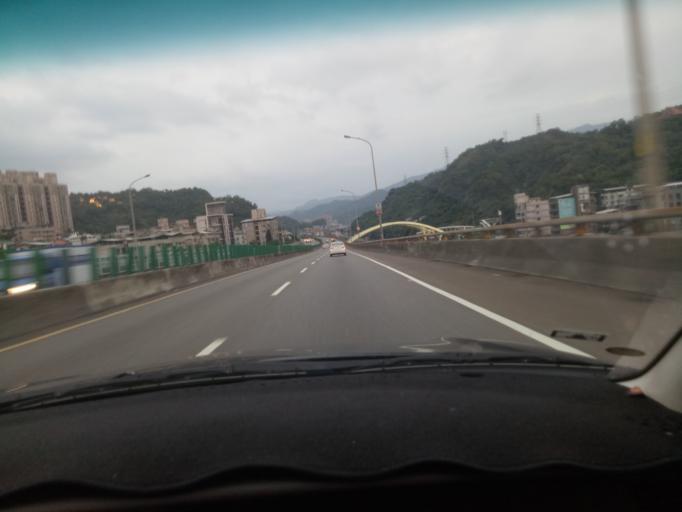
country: TW
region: Taiwan
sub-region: Keelung
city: Keelung
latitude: 25.1042
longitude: 121.7373
